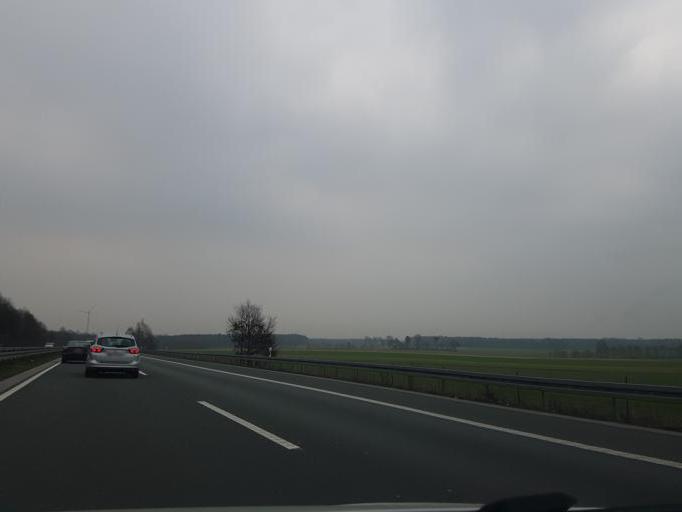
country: DE
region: North Rhine-Westphalia
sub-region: Regierungsbezirk Munster
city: Heiden
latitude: 51.7905
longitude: 6.9713
